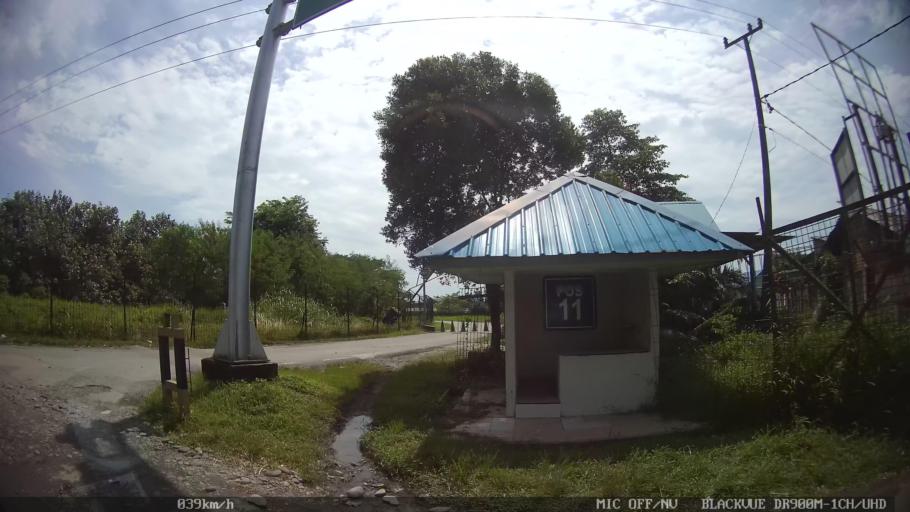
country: ID
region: North Sumatra
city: Percut
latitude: 3.6042
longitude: 98.8605
